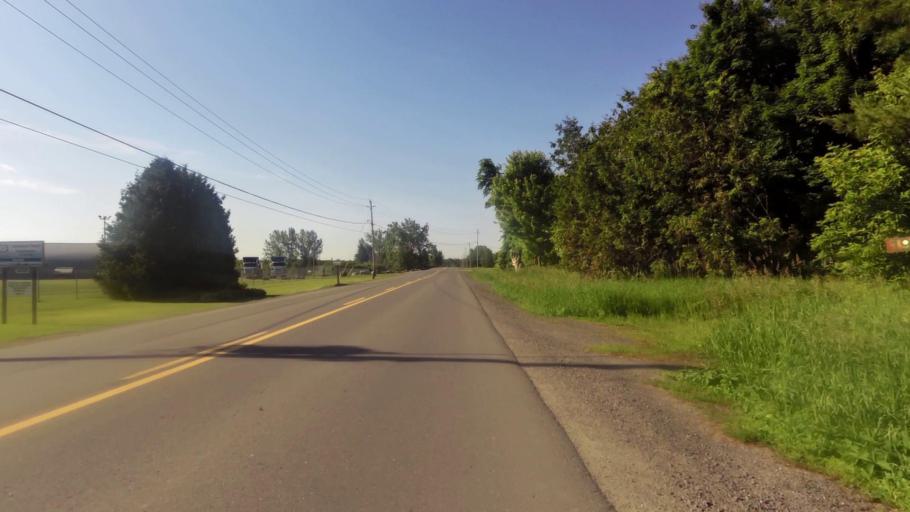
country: CA
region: Ontario
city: Ottawa
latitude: 45.2333
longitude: -75.5611
